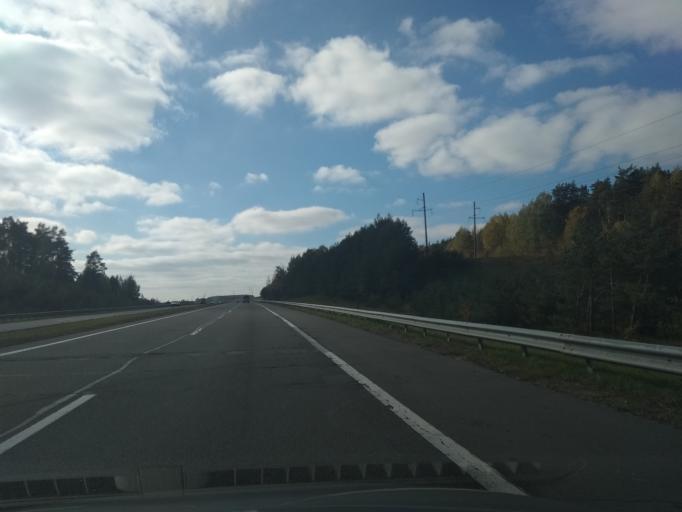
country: BY
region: Minsk
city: Novy Svyerzhan'
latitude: 53.4932
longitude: 26.6432
